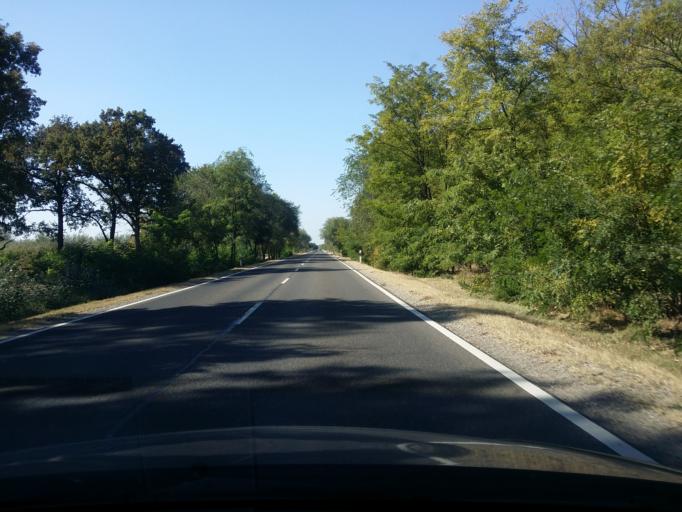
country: HU
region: Bacs-Kiskun
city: Nyarlorinc
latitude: 46.8648
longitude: 19.9082
